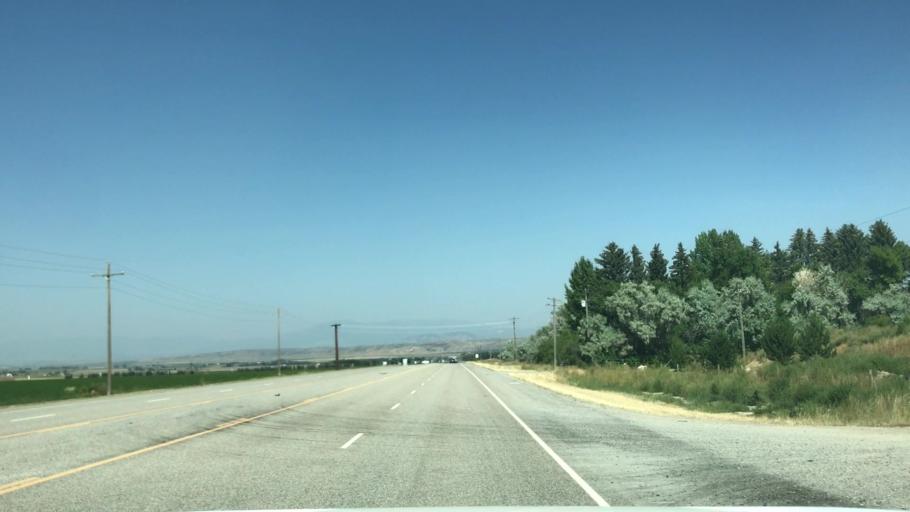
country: US
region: Montana
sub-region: Broadwater County
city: Townsend
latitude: 46.1412
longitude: -111.4766
